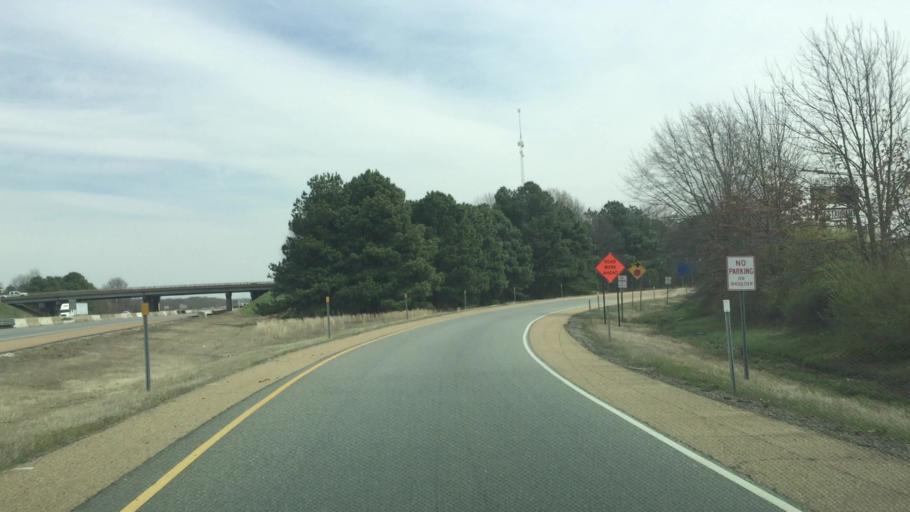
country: US
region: Arkansas
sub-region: Saint Francis County
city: Forrest City
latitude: 34.9825
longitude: -90.9070
